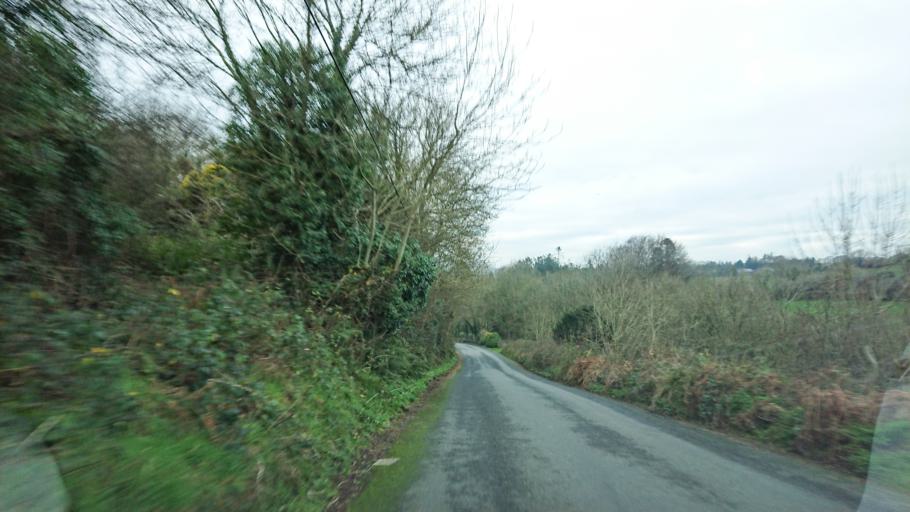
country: IE
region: Munster
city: Carrick-on-Suir
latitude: 52.2784
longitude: -7.4326
